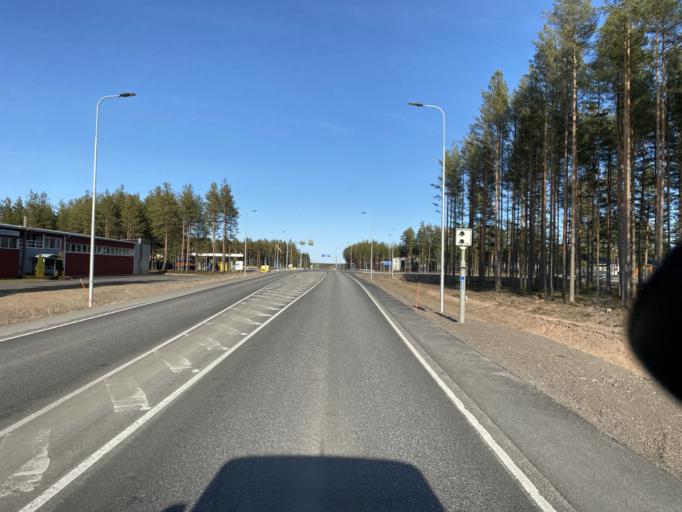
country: FI
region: Satakunta
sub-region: Rauma
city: Koeylioe
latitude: 61.1568
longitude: 22.2816
